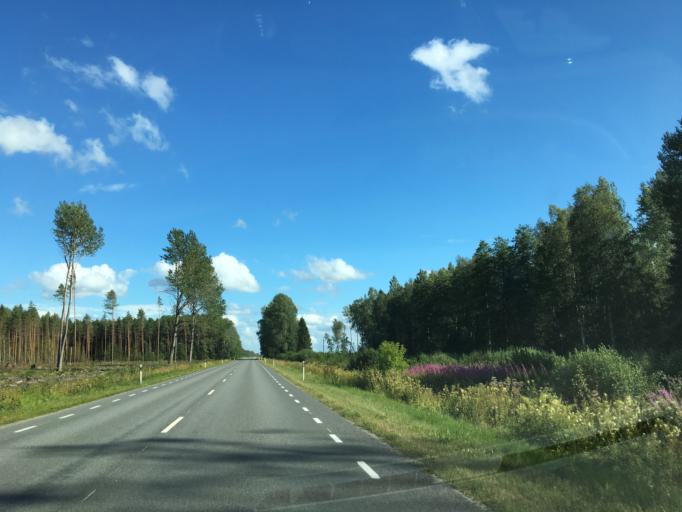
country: EE
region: Paernumaa
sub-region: Vaendra vald (alev)
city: Vandra
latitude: 58.6123
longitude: 25.1104
